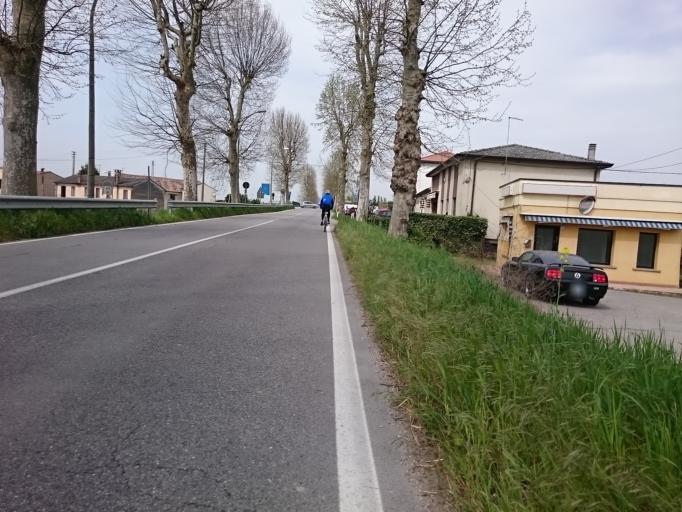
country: IT
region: Veneto
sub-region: Provincia di Padova
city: Anguillara Veneta
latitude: 45.1450
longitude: 11.8775
